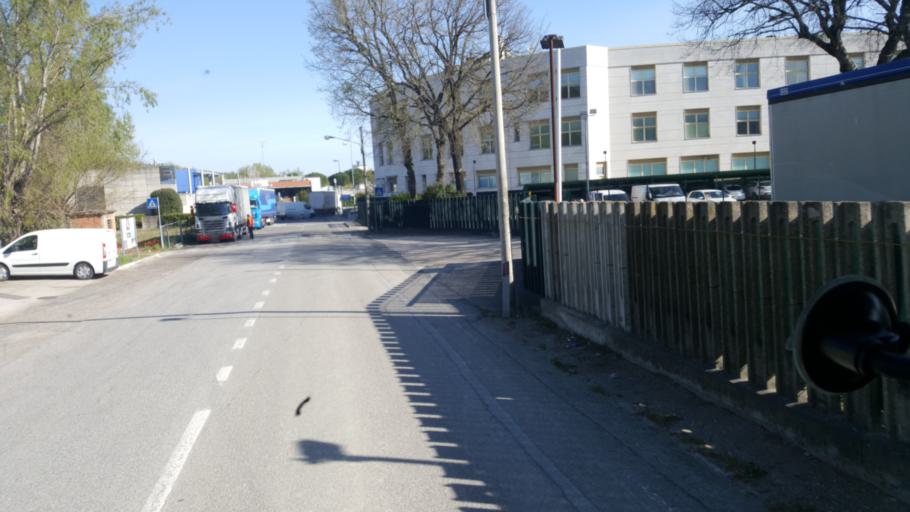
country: SM
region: Acquaviva
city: Acquaviva
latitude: 43.9511
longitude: 12.4043
